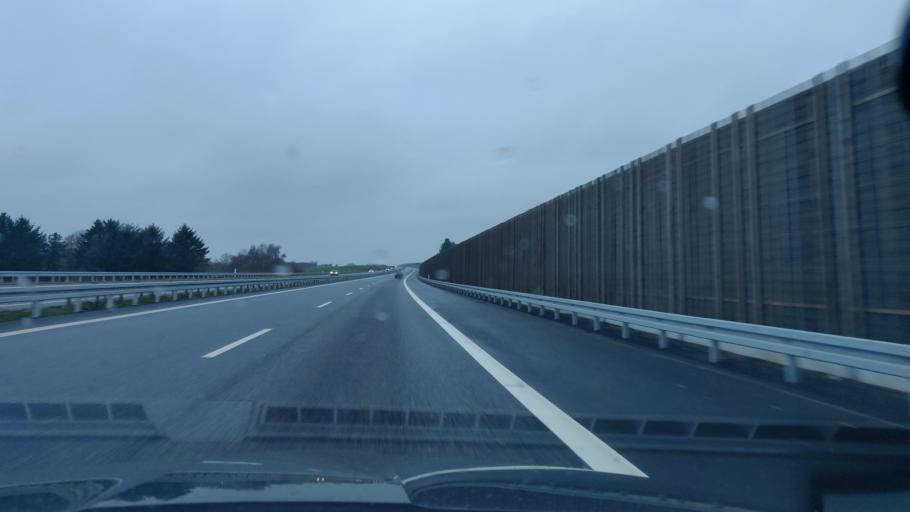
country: DK
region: Central Jutland
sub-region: Herning Kommune
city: Avlum
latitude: 56.2365
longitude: 8.8079
